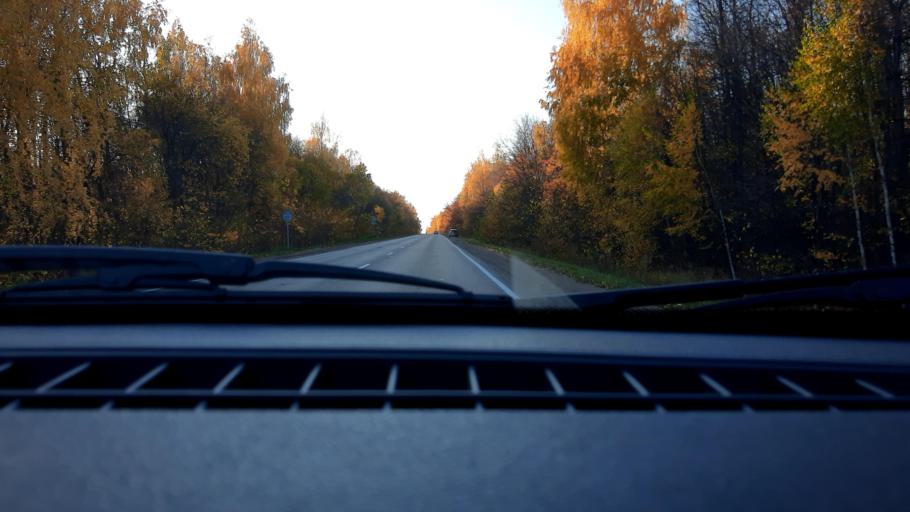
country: RU
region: Bashkortostan
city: Avdon
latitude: 54.8202
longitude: 55.7263
